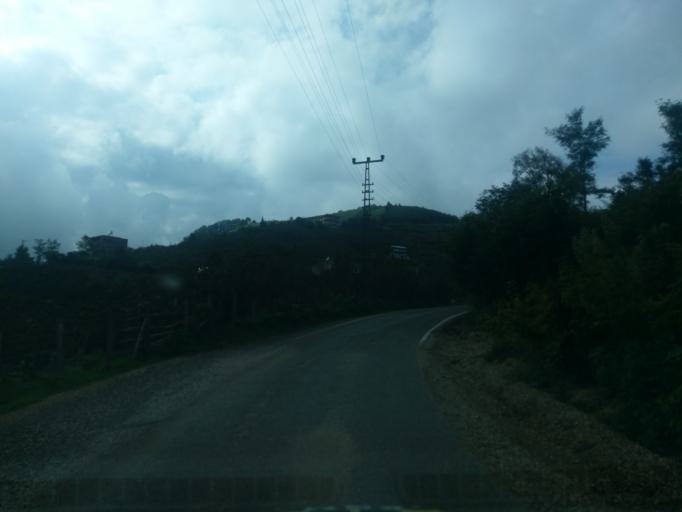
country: TR
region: Ordu
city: Camas
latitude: 40.8908
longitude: 37.6149
